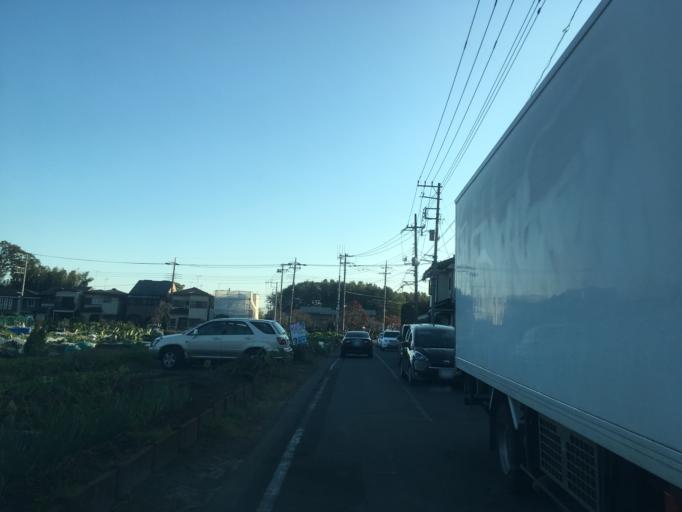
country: JP
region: Saitama
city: Tokorozawa
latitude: 35.8141
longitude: 139.4397
